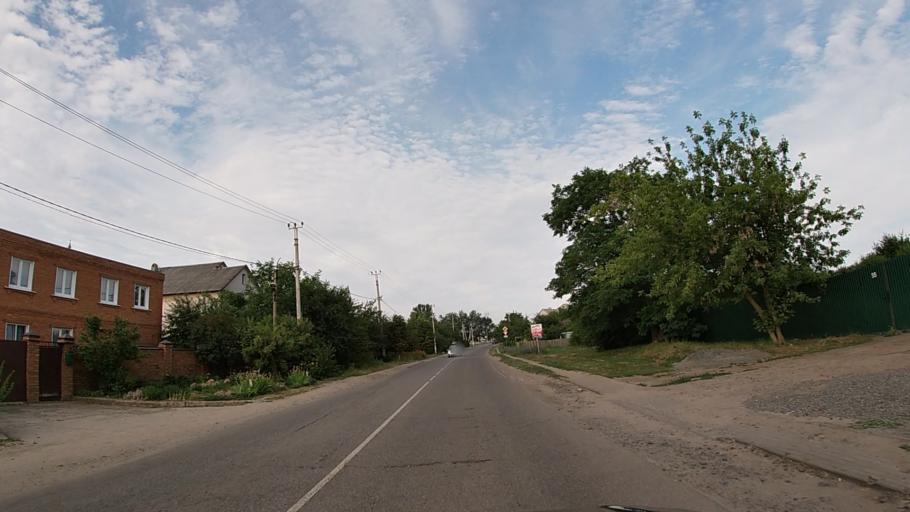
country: RU
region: Belgorod
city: Severnyy
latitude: 50.6909
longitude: 36.5612
